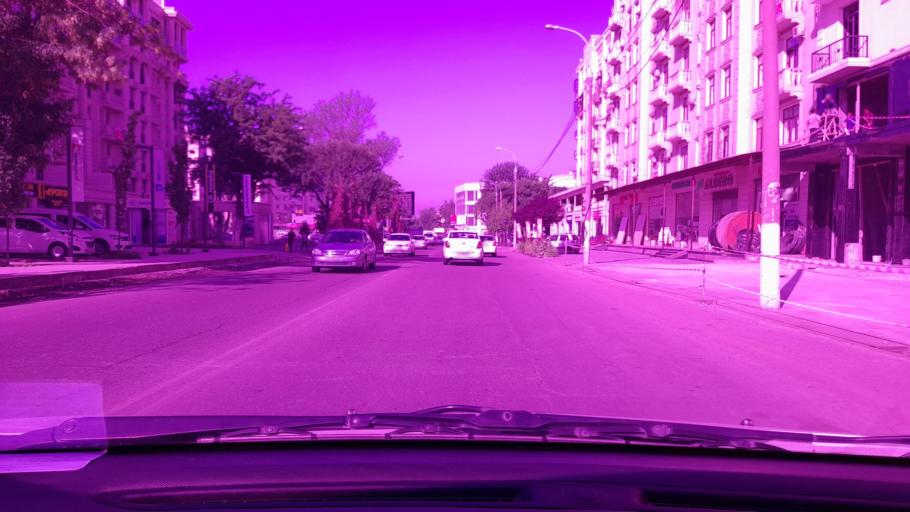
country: UZ
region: Toshkent
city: Salor
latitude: 41.3138
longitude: 69.3331
